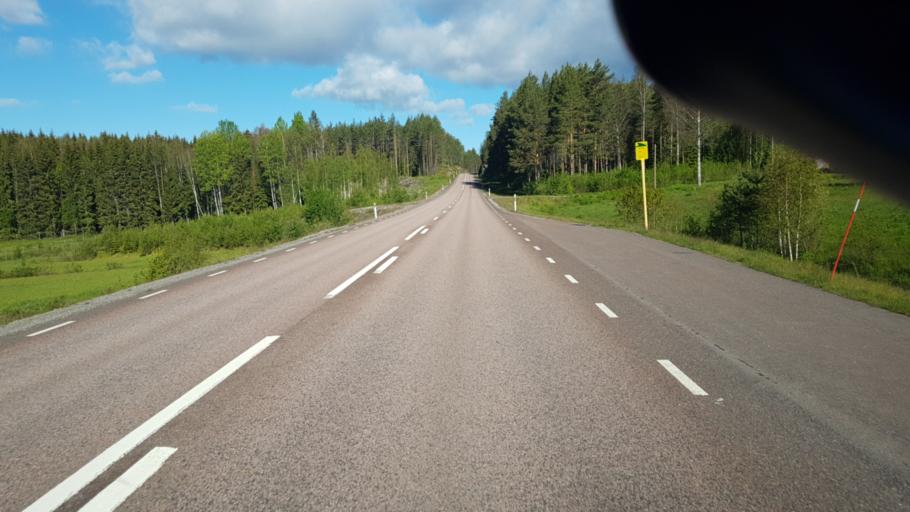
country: SE
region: Vaermland
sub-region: Arvika Kommun
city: Arvika
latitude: 59.5856
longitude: 12.6615
